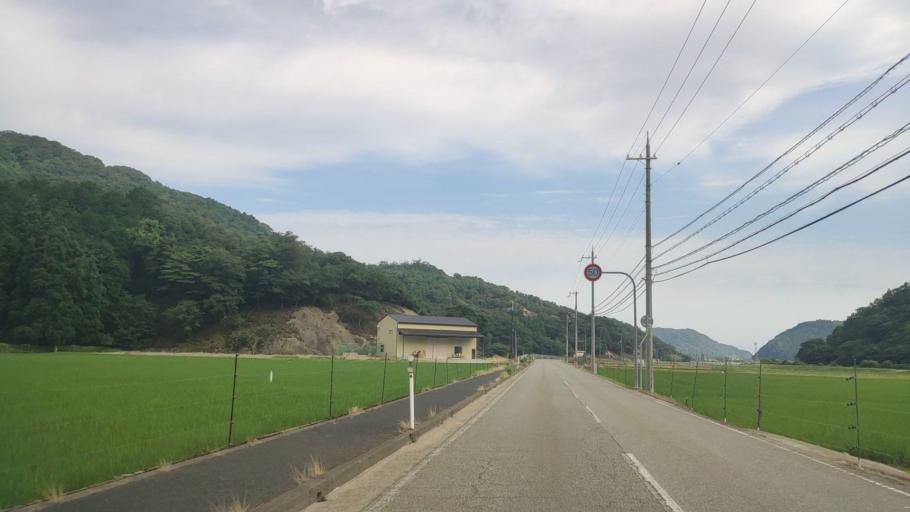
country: JP
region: Hyogo
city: Toyooka
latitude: 35.6195
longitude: 134.8421
